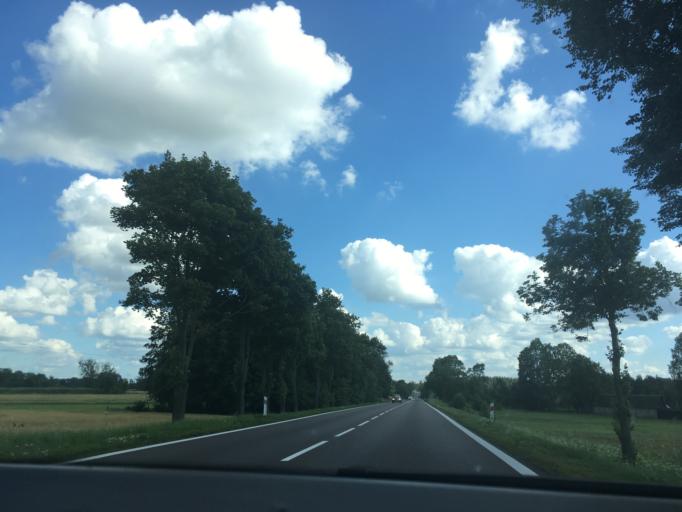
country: PL
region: Podlasie
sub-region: Powiat sokolski
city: Janow
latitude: 53.4205
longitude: 23.1114
